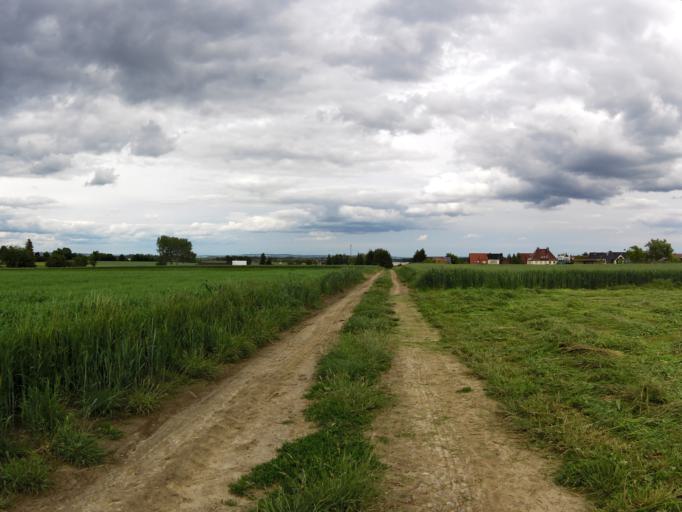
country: DE
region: Thuringia
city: Langula
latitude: 51.1545
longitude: 10.4174
